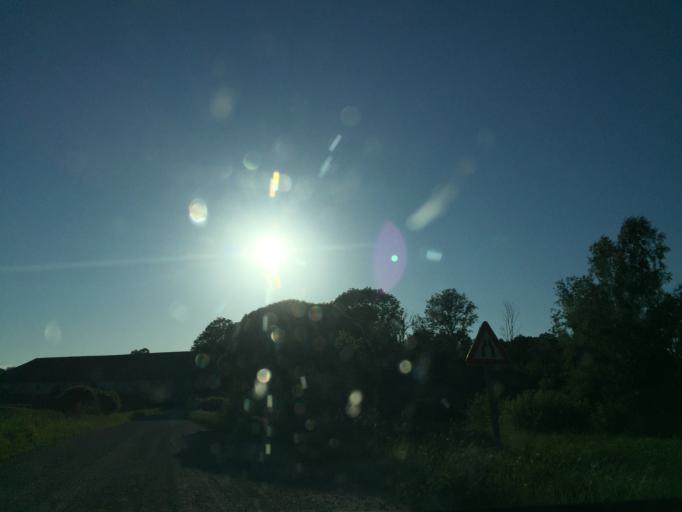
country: LV
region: Broceni
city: Broceni
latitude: 56.8652
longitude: 22.5849
